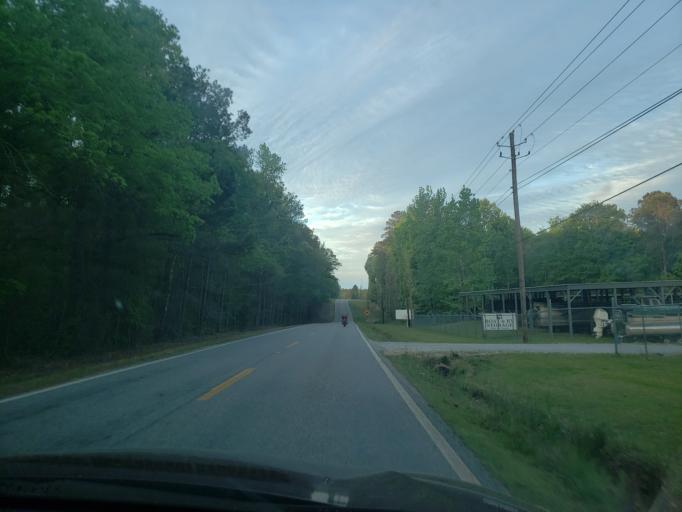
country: US
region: Alabama
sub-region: Elmore County
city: Tallassee
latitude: 32.6942
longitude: -85.8561
